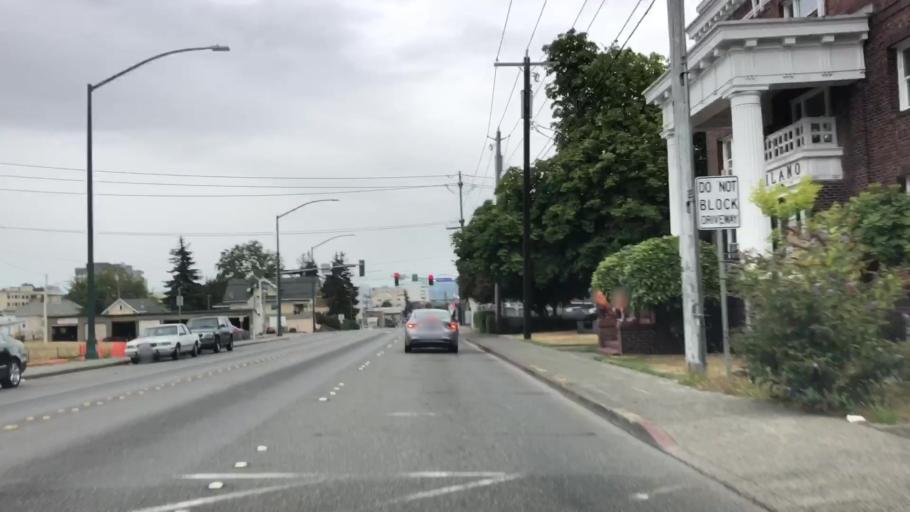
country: US
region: Washington
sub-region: Kitsap County
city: Bremerton
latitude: 47.5650
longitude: -122.6341
